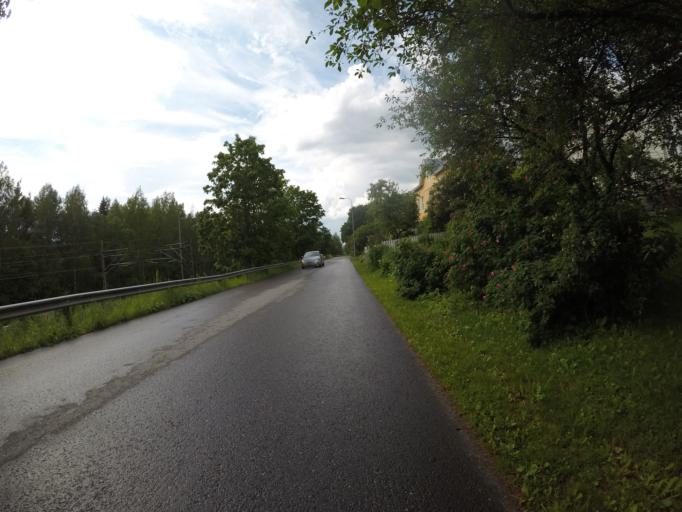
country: FI
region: Haeme
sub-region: Haemeenlinna
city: Haemeenlinna
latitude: 61.0045
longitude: 24.4741
